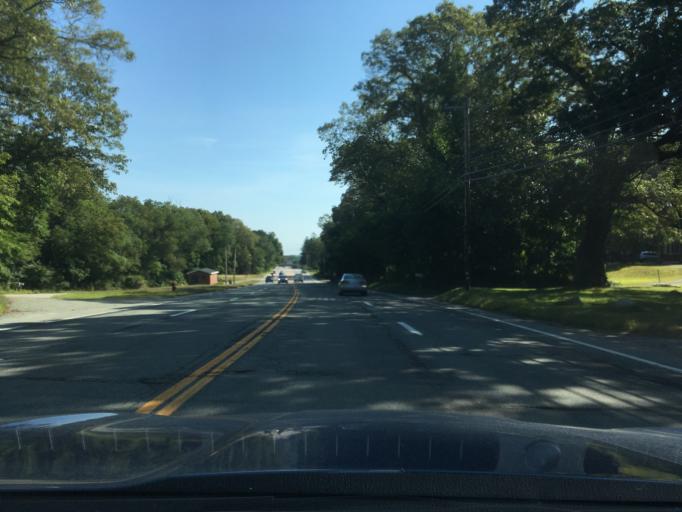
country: US
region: Rhode Island
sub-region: Washington County
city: Exeter
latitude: 41.5770
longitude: -71.5114
